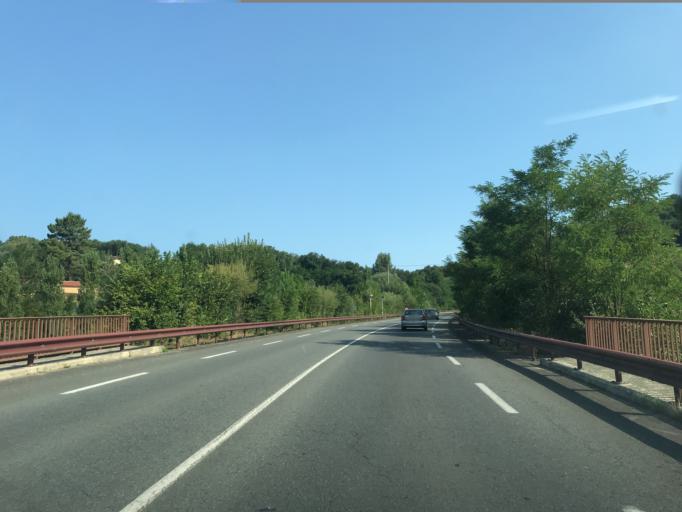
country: FR
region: Aquitaine
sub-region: Departement de la Dordogne
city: Sarlat-la-Caneda
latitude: 44.8939
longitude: 1.1993
